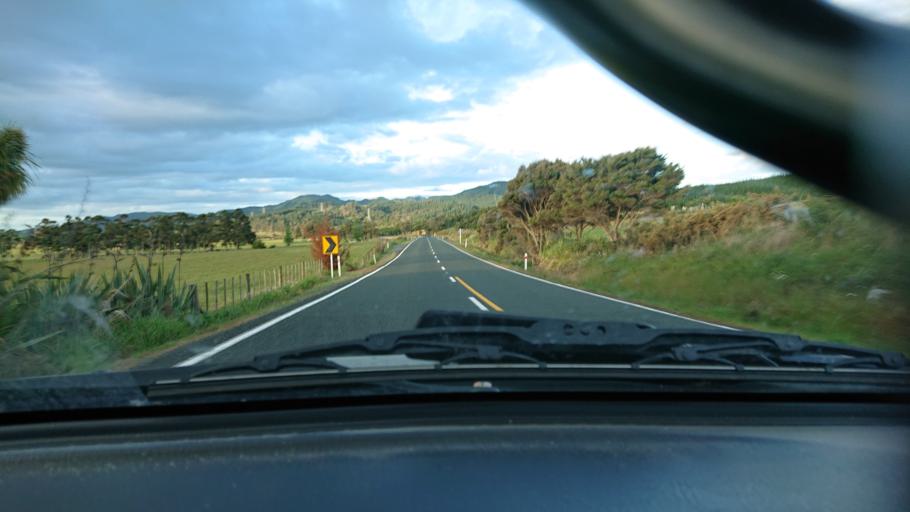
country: NZ
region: Auckland
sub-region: Auckland
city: Parakai
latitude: -36.5179
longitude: 174.4499
